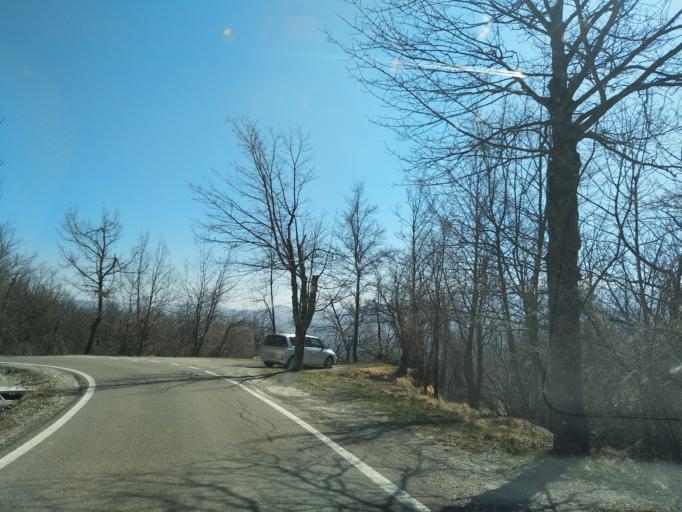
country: IT
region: Emilia-Romagna
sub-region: Provincia di Reggio Emilia
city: Castelnovo ne'Monti
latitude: 44.4184
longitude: 10.4072
